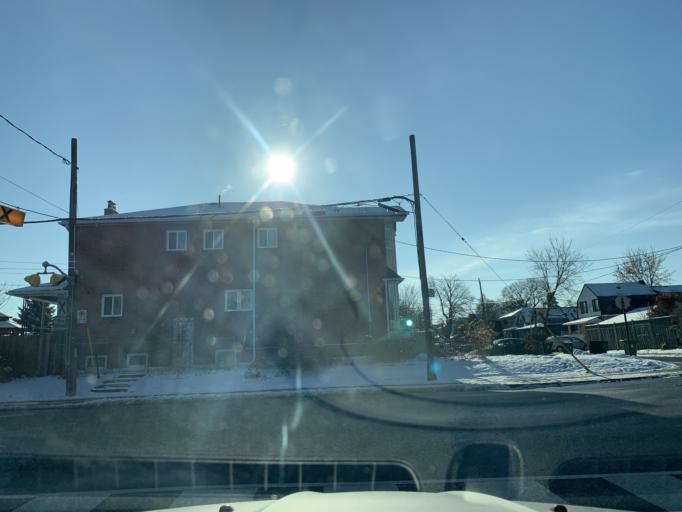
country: CA
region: Ontario
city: Toronto
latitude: 43.6832
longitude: -79.4891
